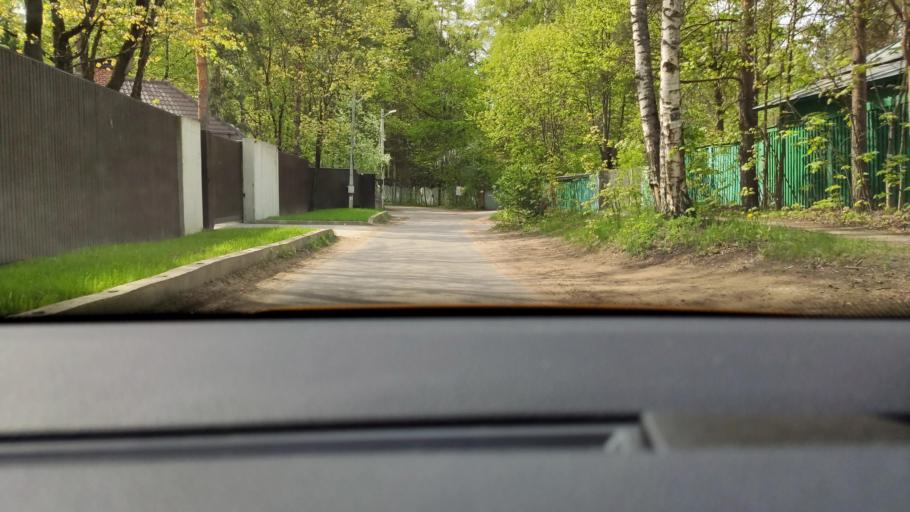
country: RU
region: Moskovskaya
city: Nikolina Gora
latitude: 55.7364
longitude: 37.0342
